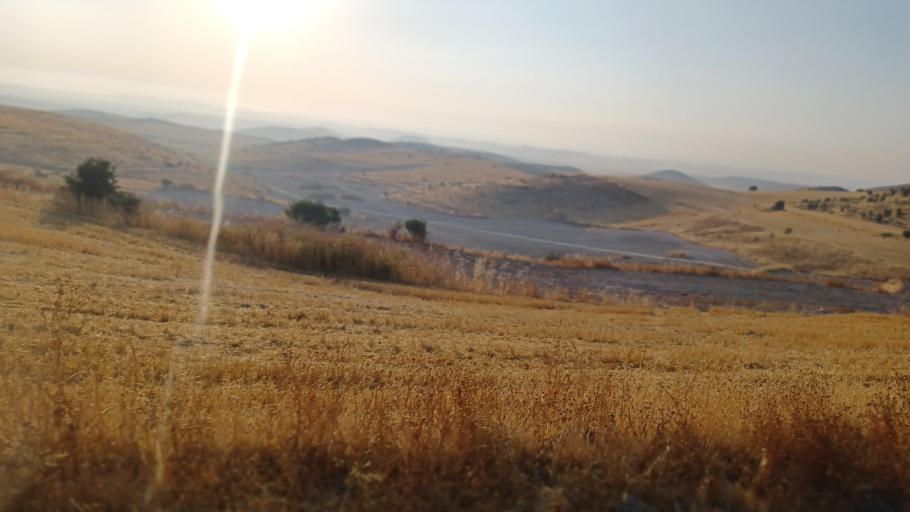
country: CY
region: Larnaka
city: Psevdas
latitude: 34.9081
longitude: 33.4923
